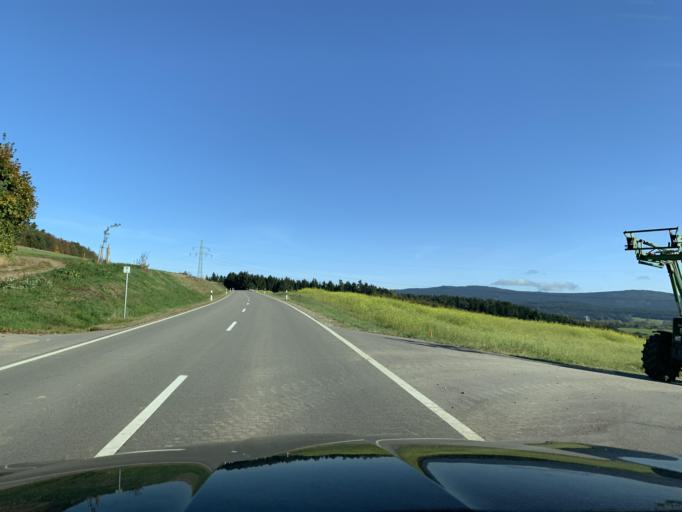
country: DE
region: Bavaria
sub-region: Upper Palatinate
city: Winklarn
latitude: 49.4110
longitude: 12.4654
